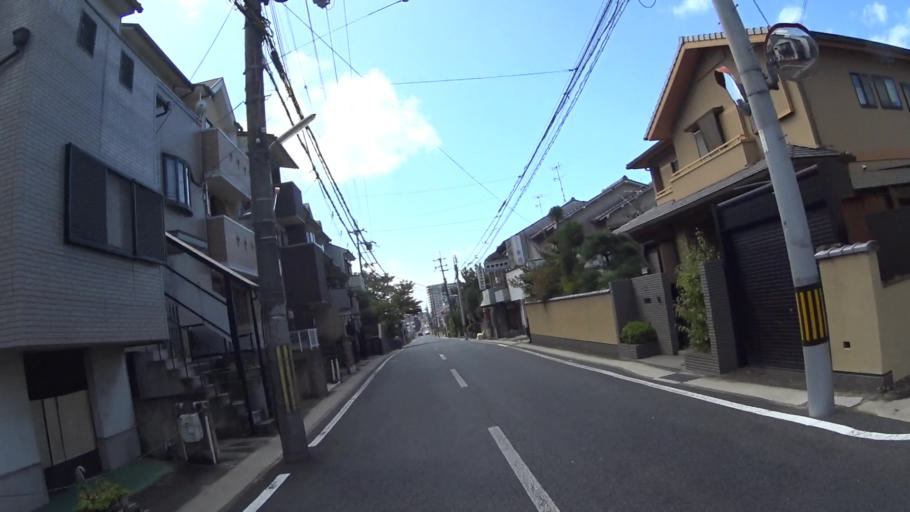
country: JP
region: Kyoto
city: Uji
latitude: 34.9371
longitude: 135.8052
